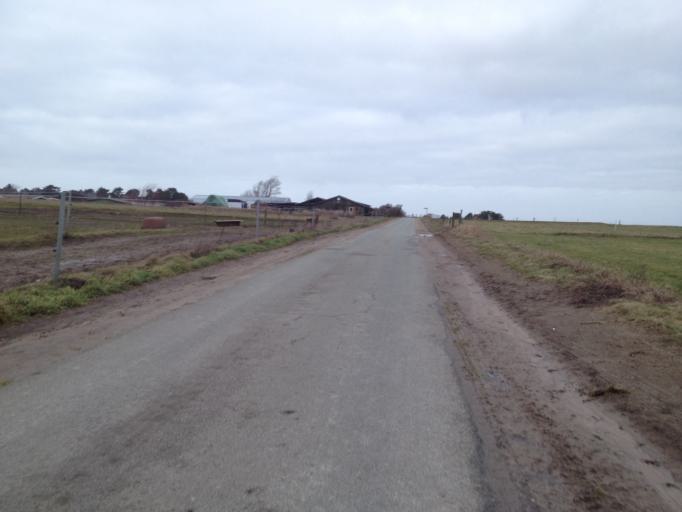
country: DE
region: Schleswig-Holstein
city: Norddorf
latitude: 54.6741
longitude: 8.3411
